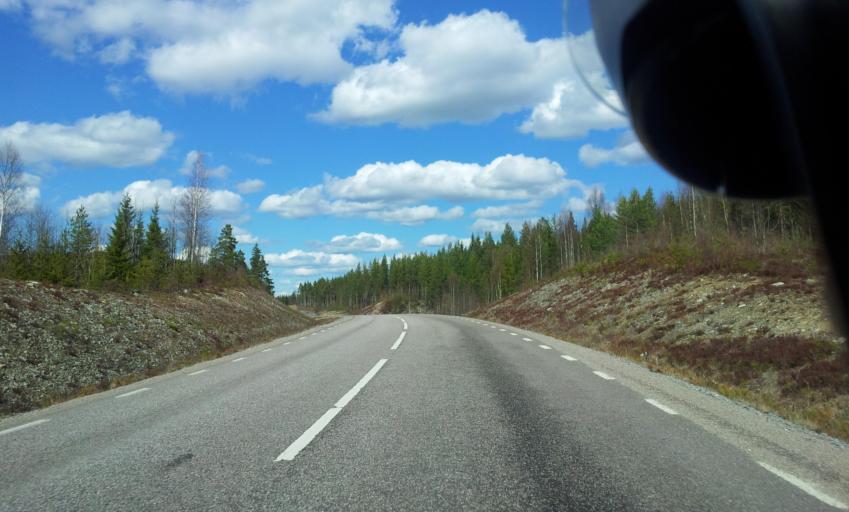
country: SE
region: Gaevleborg
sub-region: Ovanakers Kommun
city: Edsbyn
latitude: 61.2164
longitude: 15.8770
